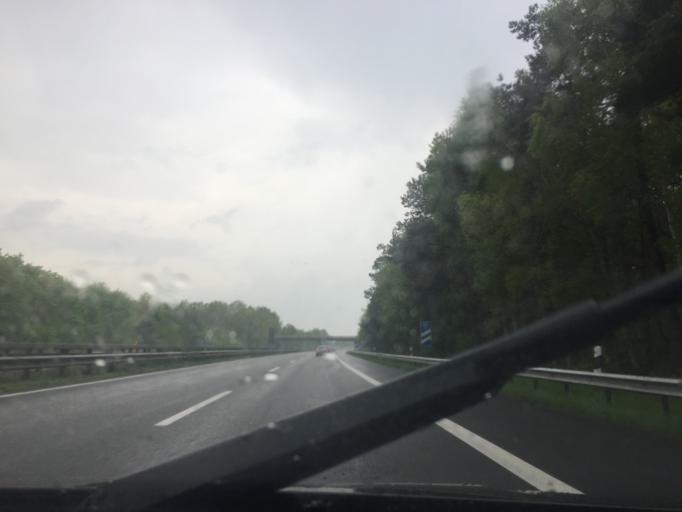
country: DE
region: Lower Saxony
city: Bad Zwischenahn
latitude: 53.2134
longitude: 8.0573
